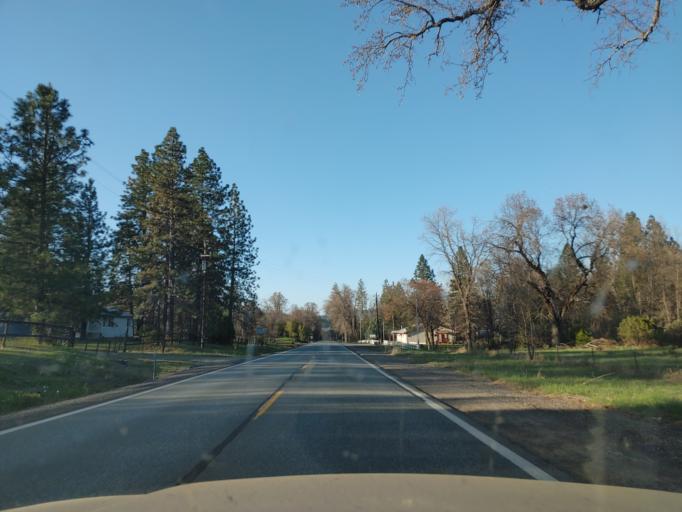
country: US
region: California
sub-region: Shasta County
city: Burney
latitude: 40.8100
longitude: -121.9395
